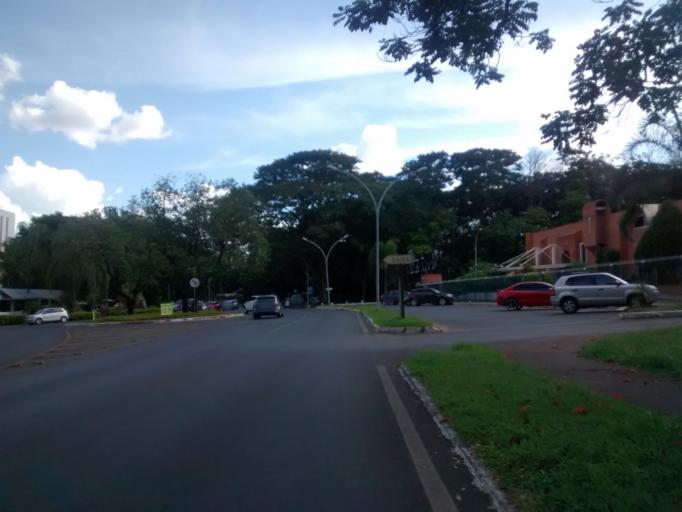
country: BR
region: Federal District
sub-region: Brasilia
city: Brasilia
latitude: -15.8057
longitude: -47.8938
